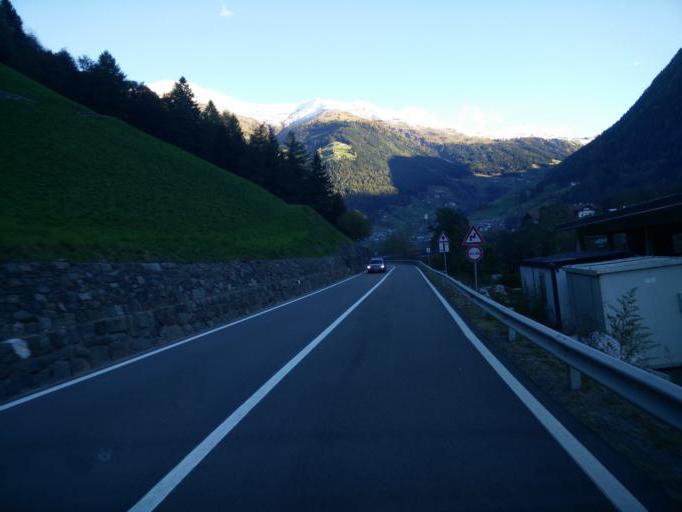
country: IT
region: Trentino-Alto Adige
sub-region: Bolzano
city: San Martino in Passiria
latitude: 46.7965
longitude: 11.2333
